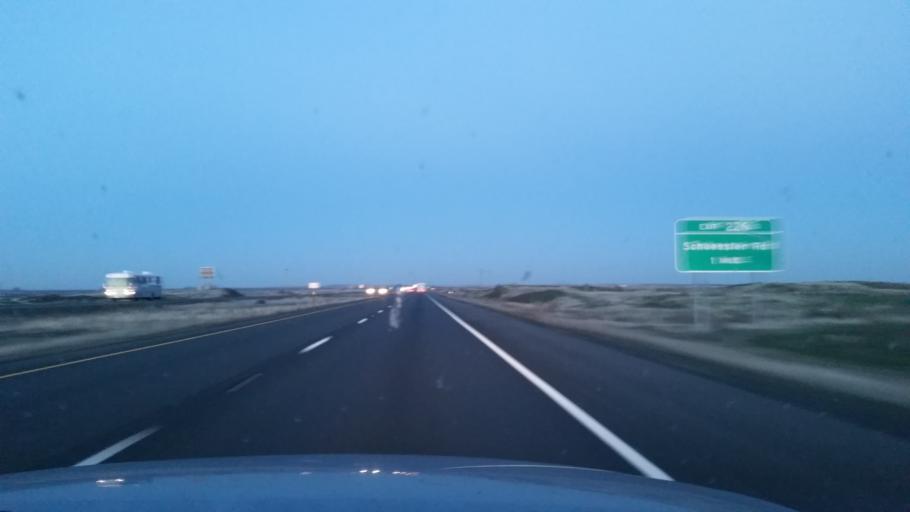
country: US
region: Washington
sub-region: Adams County
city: Ritzville
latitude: 47.1495
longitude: -118.3182
